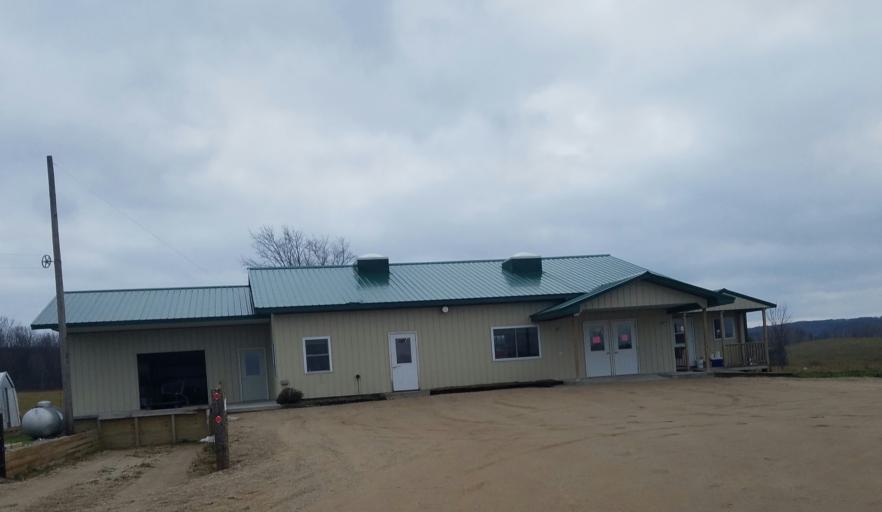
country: US
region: Michigan
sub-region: Wexford County
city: Manton
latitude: 44.4103
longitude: -85.4728
